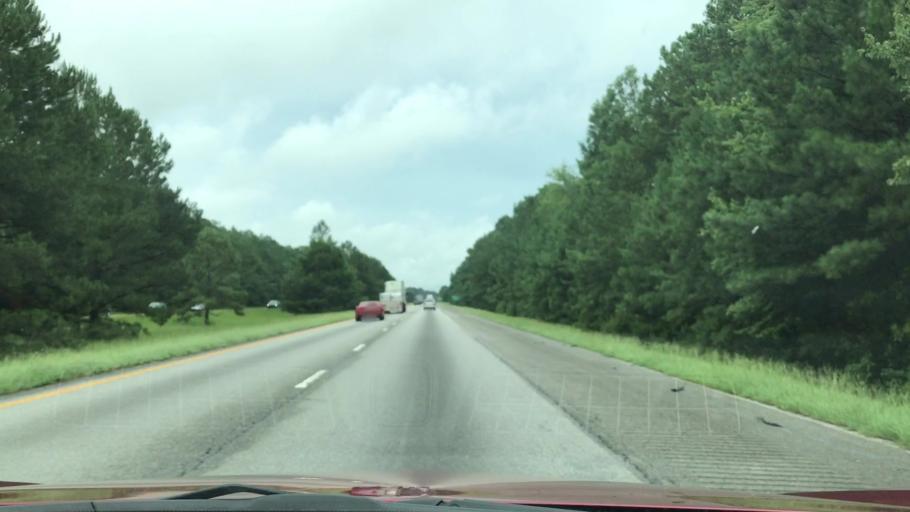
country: US
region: South Carolina
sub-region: Orangeburg County
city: Brookdale
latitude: 33.4188
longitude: -80.6750
